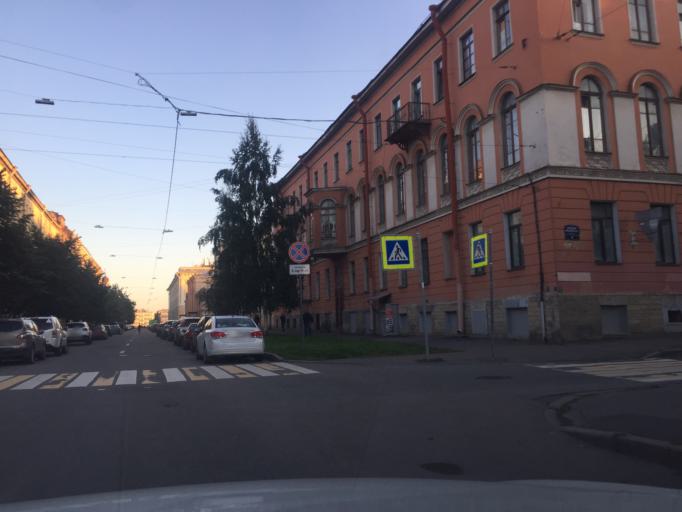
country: RU
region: St.-Petersburg
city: Saint Petersburg
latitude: 59.9406
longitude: 30.2884
